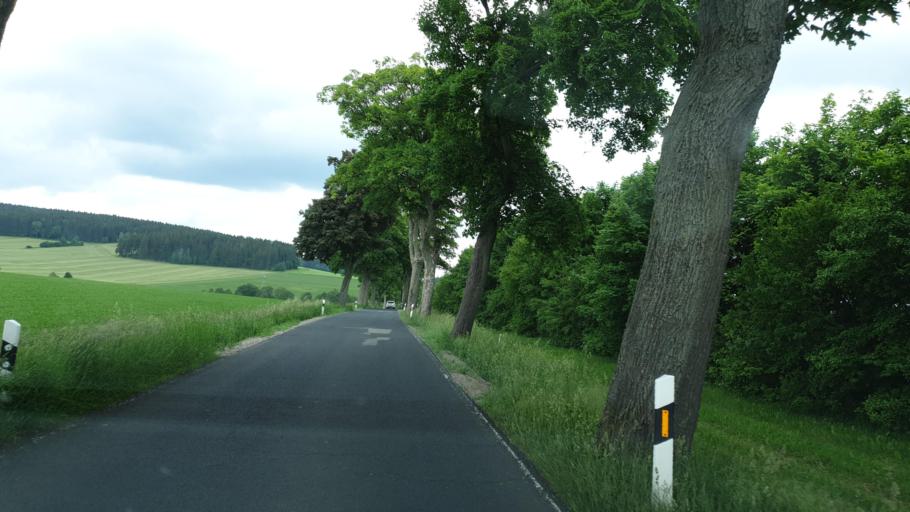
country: DE
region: Saxony
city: Marienberg
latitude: 50.6828
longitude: 13.1787
